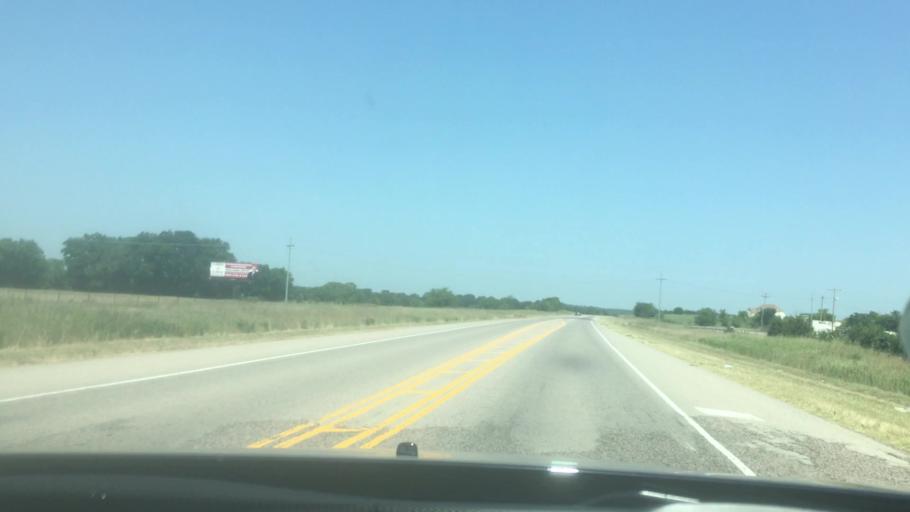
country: US
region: Oklahoma
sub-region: Pontotoc County
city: Ada
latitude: 34.7092
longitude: -96.6149
